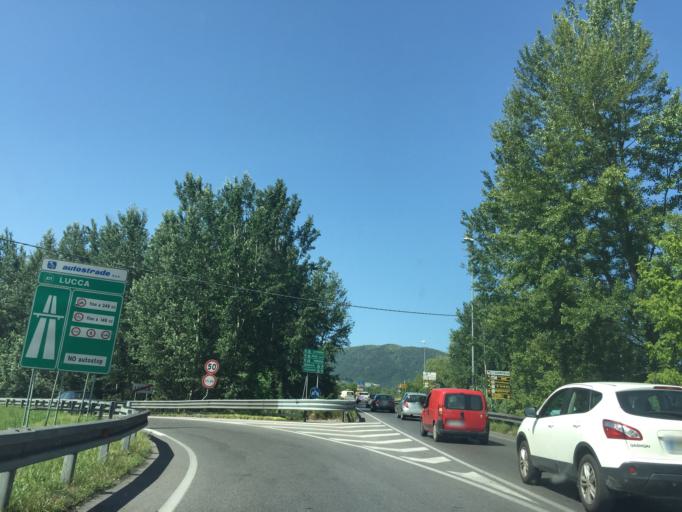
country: IT
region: Tuscany
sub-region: Provincia di Lucca
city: Lucca
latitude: 43.8319
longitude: 10.4931
